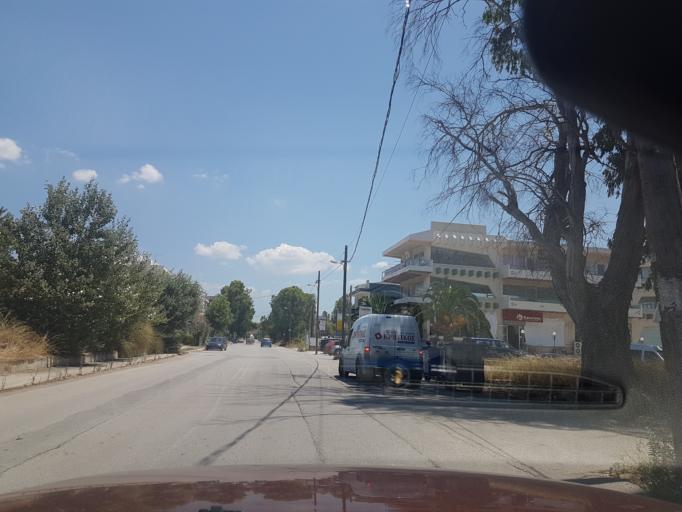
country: GR
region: Central Greece
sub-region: Nomos Evvoias
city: Chalkida
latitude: 38.4697
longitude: 23.6172
